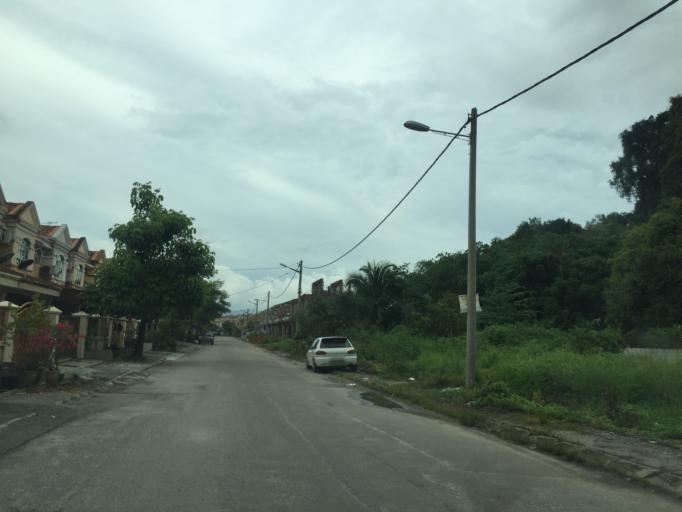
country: MY
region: Perak
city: Ipoh
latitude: 4.5624
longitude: 101.1245
